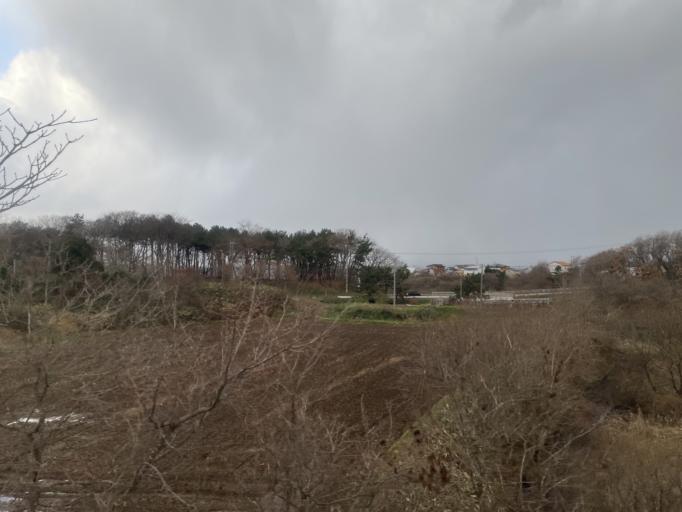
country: JP
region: Aomori
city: Mutsu
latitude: 41.1291
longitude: 141.2721
